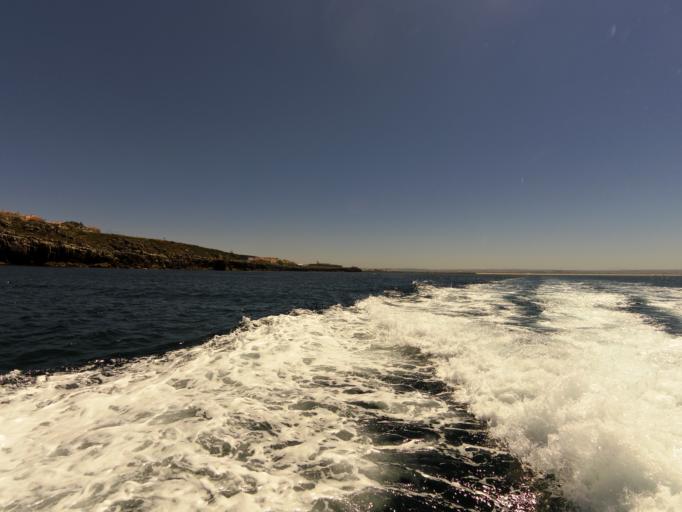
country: PT
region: Leiria
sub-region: Peniche
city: Peniche
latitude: 39.3517
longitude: -9.3941
